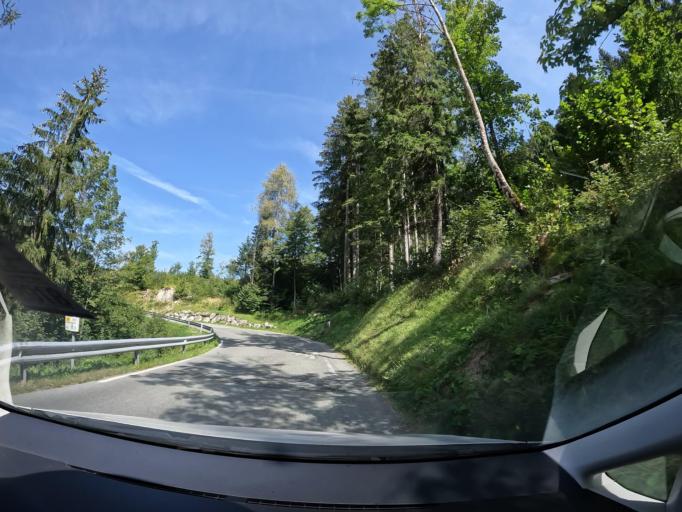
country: AT
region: Carinthia
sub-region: Politischer Bezirk Klagenfurt Land
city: Schiefling am See
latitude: 46.5770
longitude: 14.0781
